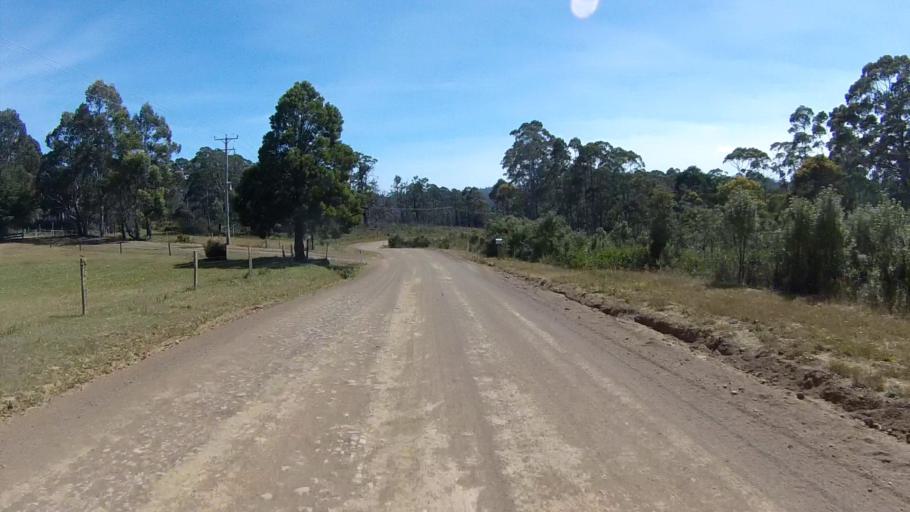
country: AU
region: Tasmania
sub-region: Sorell
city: Sorell
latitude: -42.7301
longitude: 147.7392
